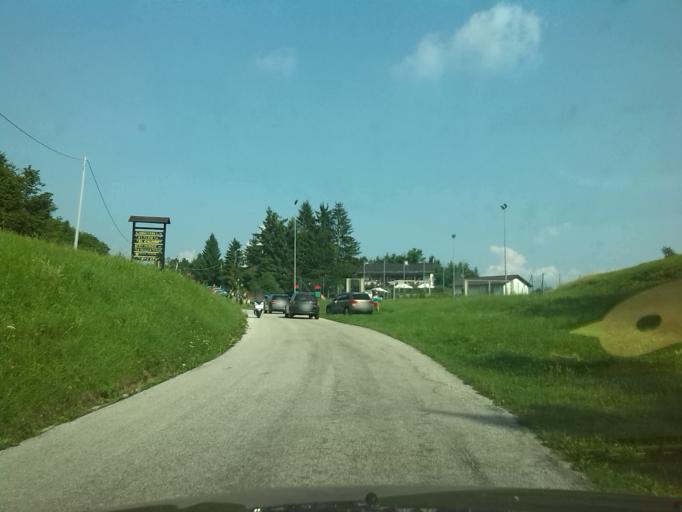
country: IT
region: Friuli Venezia Giulia
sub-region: Provincia di Udine
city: Cras
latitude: 46.1801
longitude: 13.6586
